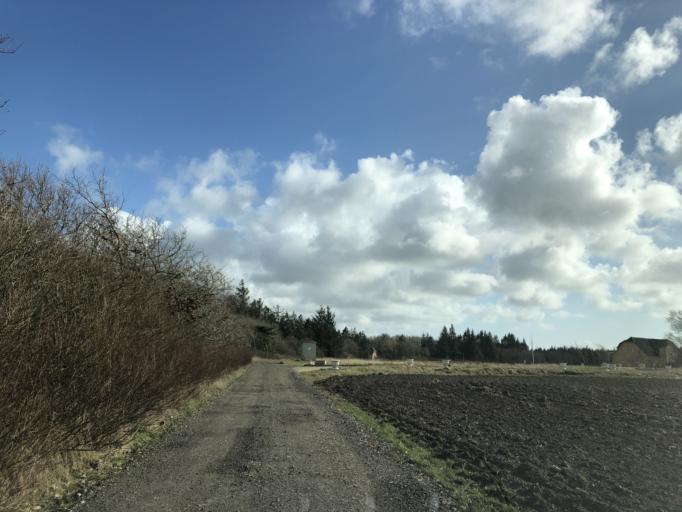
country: DK
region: Central Jutland
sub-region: Holstebro Kommune
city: Ulfborg
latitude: 56.2796
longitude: 8.3472
